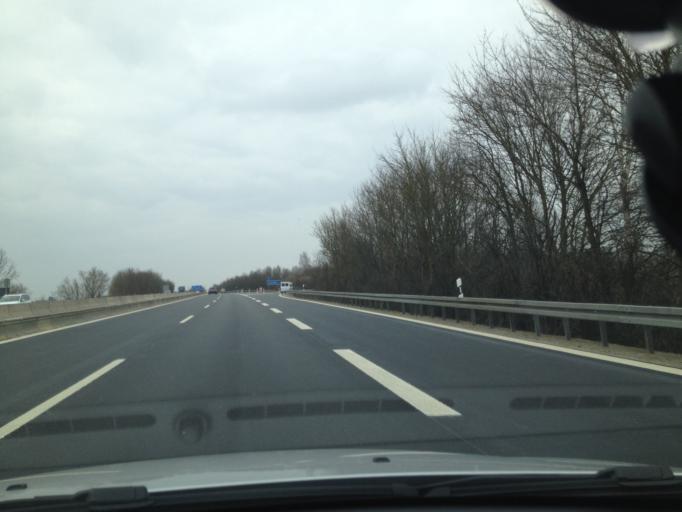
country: DE
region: Bavaria
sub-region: Regierungsbezirk Unterfranken
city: Biebelried
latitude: 49.7592
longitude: 10.1057
